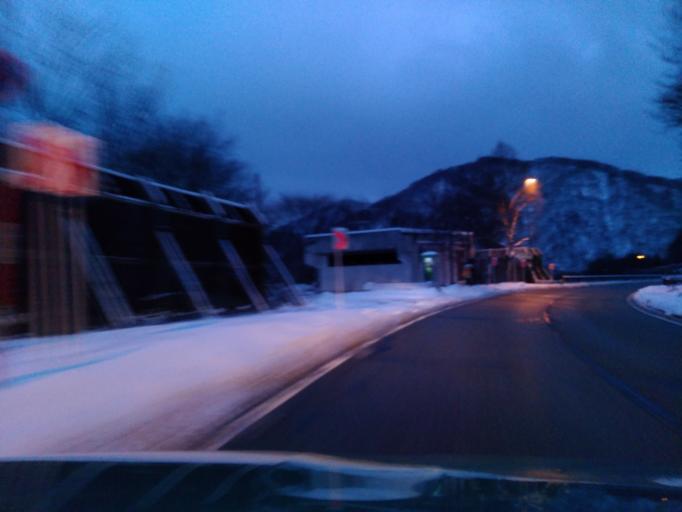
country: JP
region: Iwate
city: Shizukuishi
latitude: 39.6906
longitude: 140.7966
